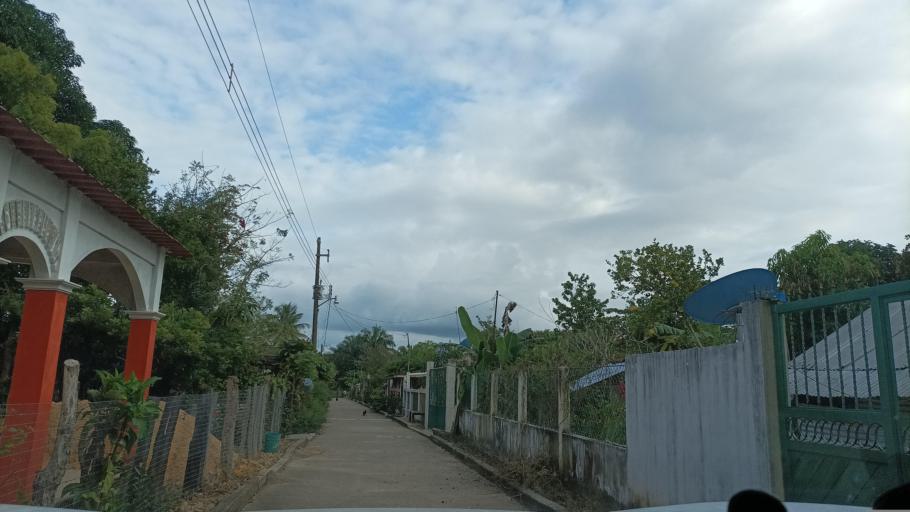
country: MX
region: Veracruz
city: Oluta
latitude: 17.8921
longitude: -94.8693
